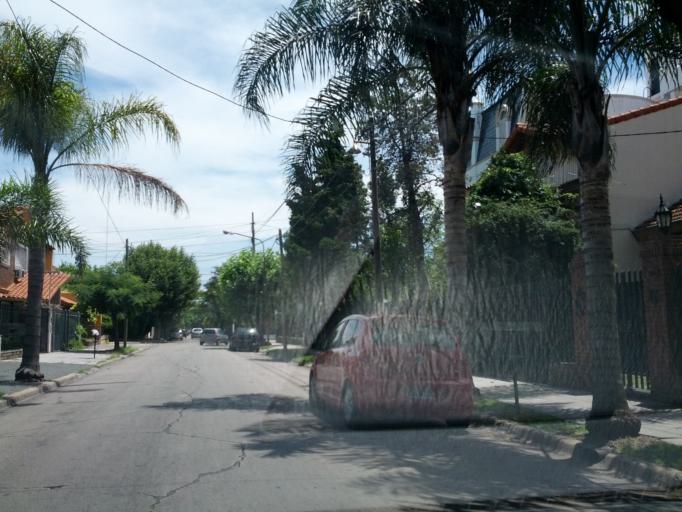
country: AR
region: Buenos Aires
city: San Justo
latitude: -34.6457
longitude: -58.5739
